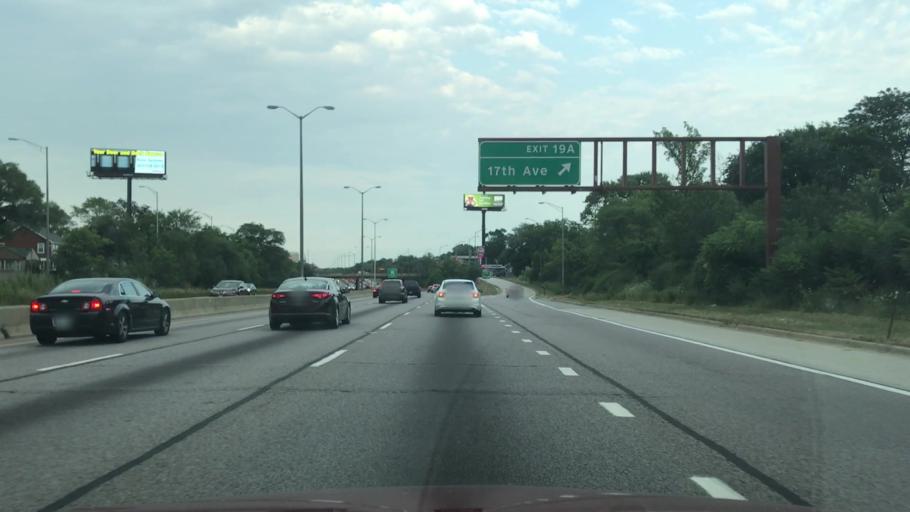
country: US
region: Illinois
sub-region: Cook County
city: Broadview
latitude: 41.8710
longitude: -87.8573
